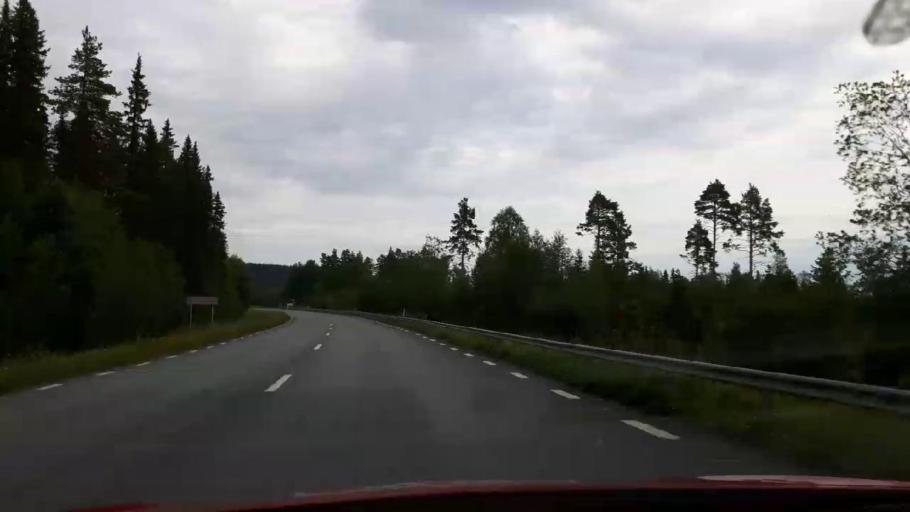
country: SE
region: Jaemtland
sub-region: Stroemsunds Kommun
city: Stroemsund
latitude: 63.5416
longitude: 15.3667
